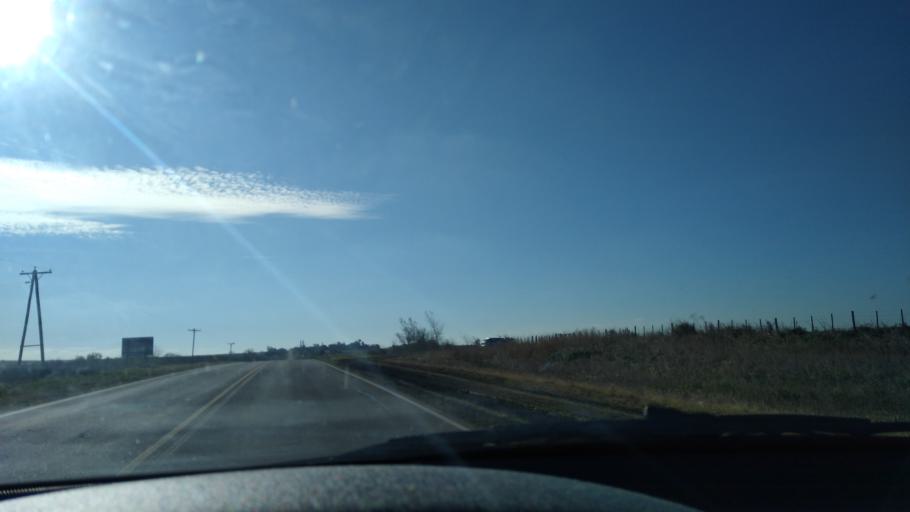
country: AR
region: Entre Rios
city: Aranguren
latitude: -32.3798
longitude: -60.3374
